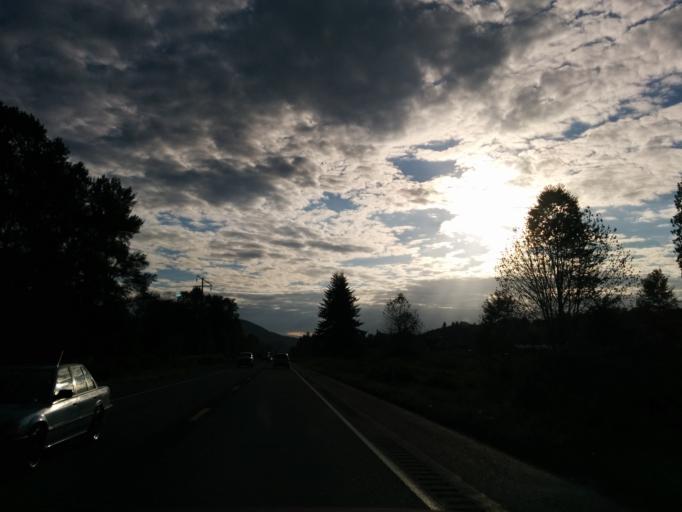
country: US
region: Washington
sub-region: Snohomish County
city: Sultan
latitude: 47.8559
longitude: -121.8387
